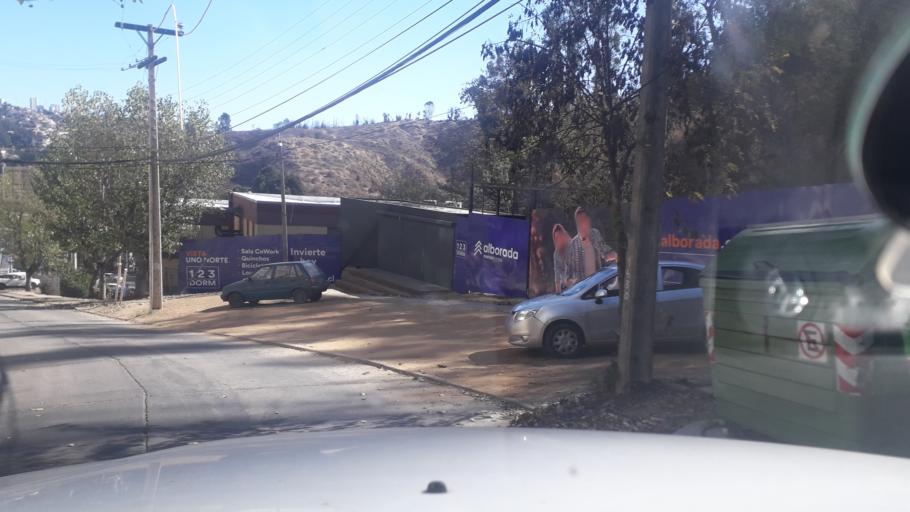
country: CL
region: Valparaiso
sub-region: Provincia de Valparaiso
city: Vina del Mar
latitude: -33.0366
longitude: -71.5147
